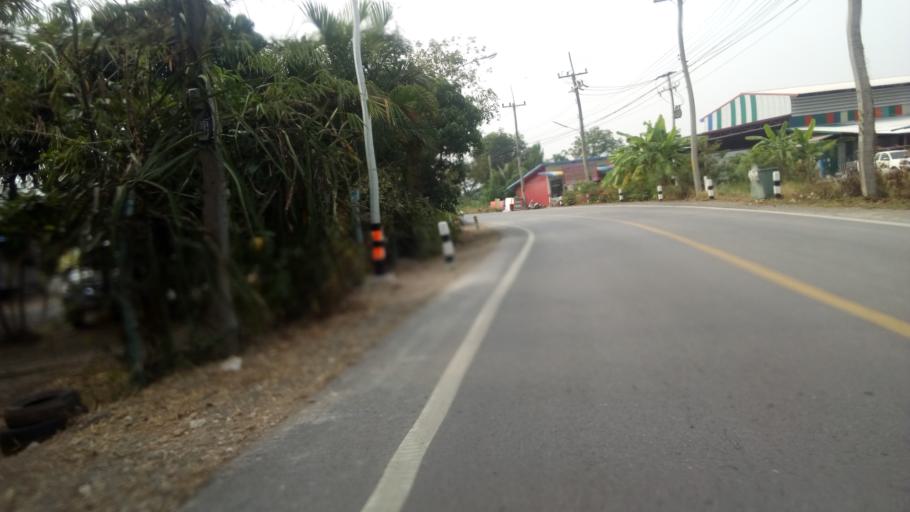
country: TH
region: Pathum Thani
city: Ban Rangsit
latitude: 14.0506
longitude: 100.8255
